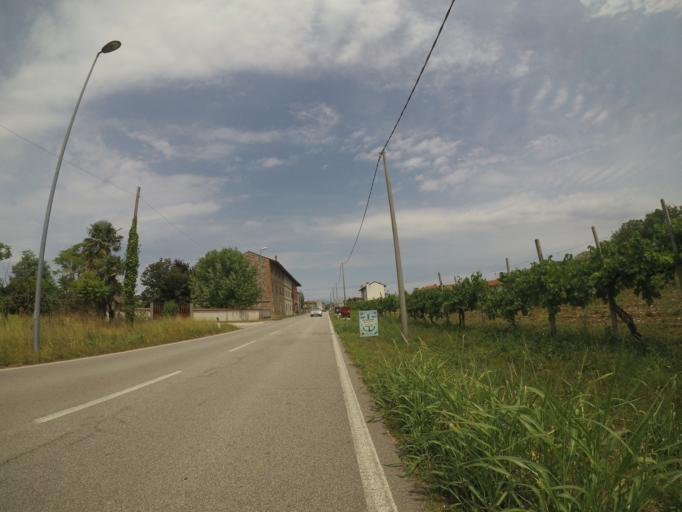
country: IT
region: Friuli Venezia Giulia
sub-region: Provincia di Udine
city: Sedegliano
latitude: 45.9917
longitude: 12.9978
